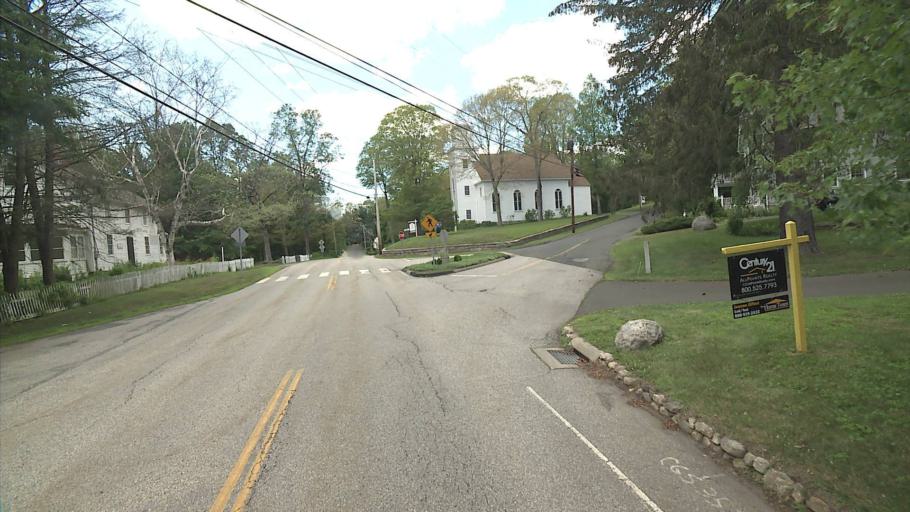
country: US
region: Connecticut
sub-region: Middlesex County
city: East Hampton
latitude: 41.5539
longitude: -72.5503
